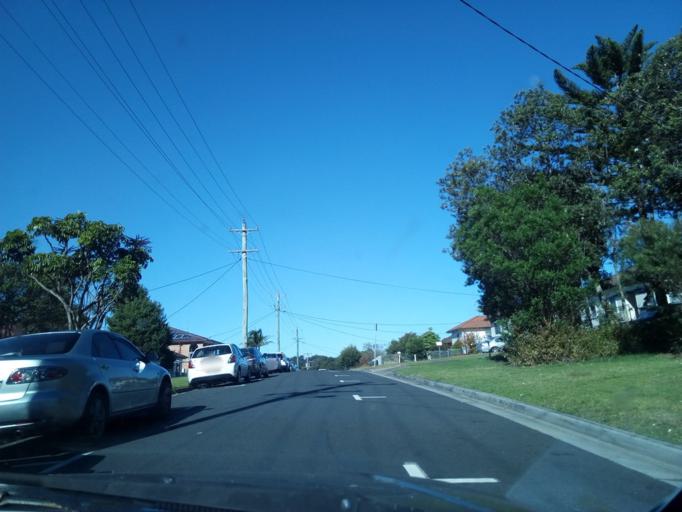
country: AU
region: New South Wales
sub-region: Wollongong
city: Gwynneville
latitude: -34.4096
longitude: 150.8813
